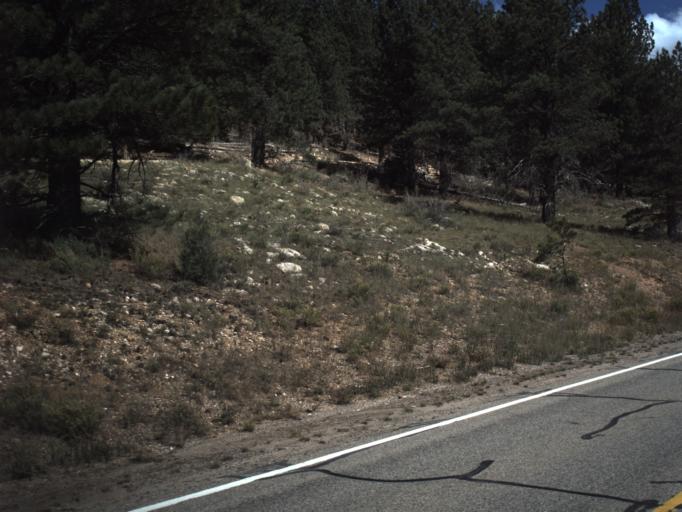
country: US
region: Utah
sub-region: Iron County
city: Parowan
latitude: 37.5228
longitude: -112.6569
